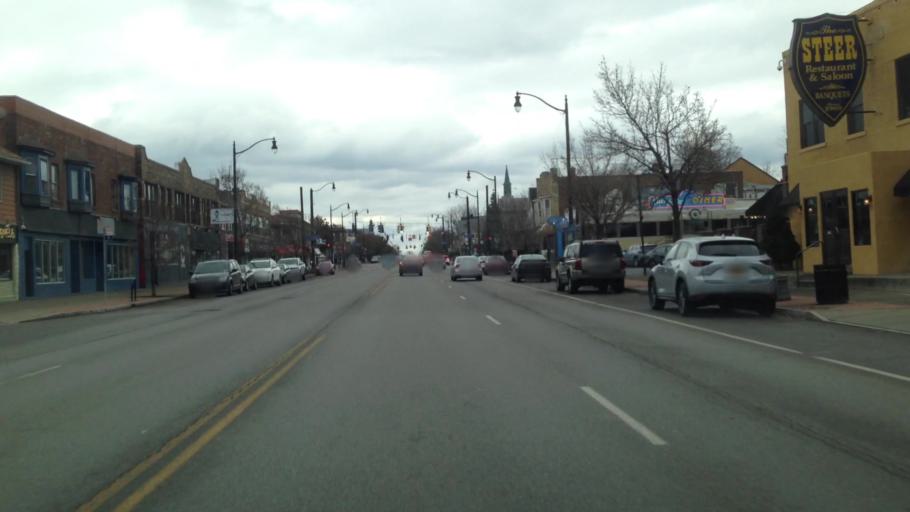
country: US
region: New York
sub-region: Erie County
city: Eggertsville
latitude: 42.9498
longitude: -78.8273
